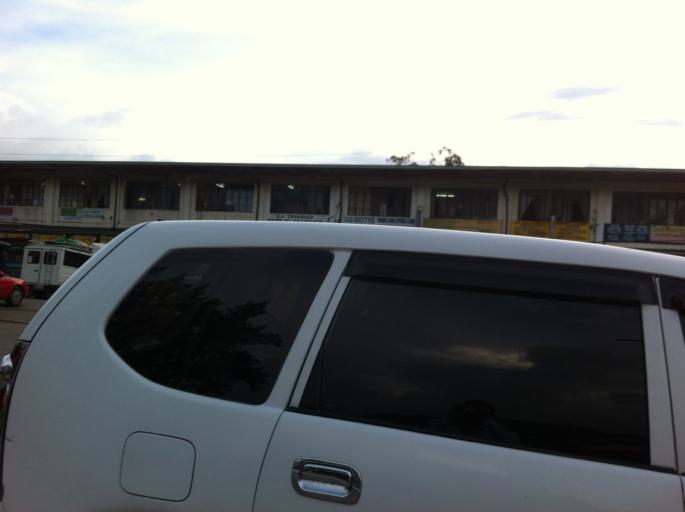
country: PH
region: Cordillera
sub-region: Province of Benguet
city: La Trinidad
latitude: 16.4479
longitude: 120.5901
